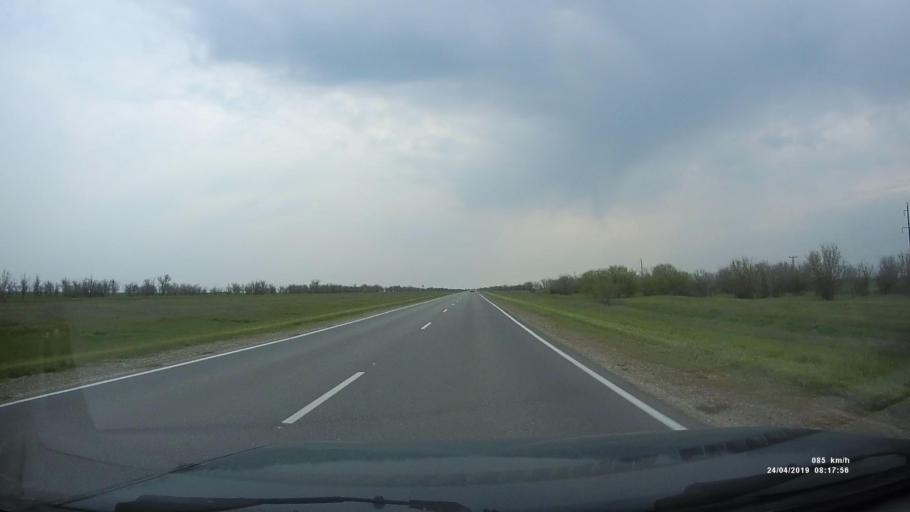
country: RU
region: Kalmykiya
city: Priyutnoye
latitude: 46.0990
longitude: 43.6388
